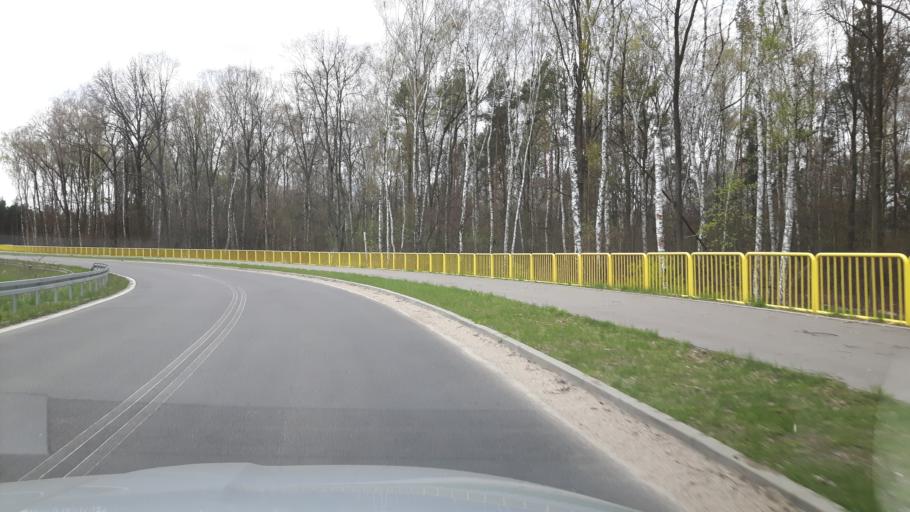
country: PL
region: Masovian Voivodeship
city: Zielonka
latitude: 52.3321
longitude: 21.1498
